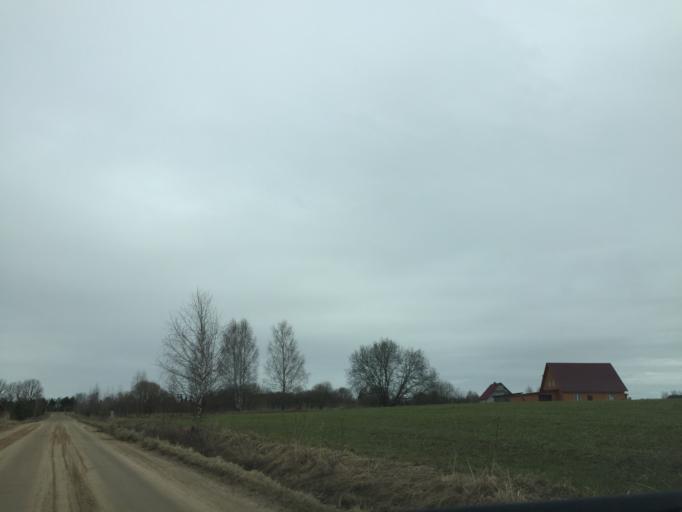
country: LV
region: Daugavpils
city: Daugavpils
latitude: 55.9153
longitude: 26.7380
